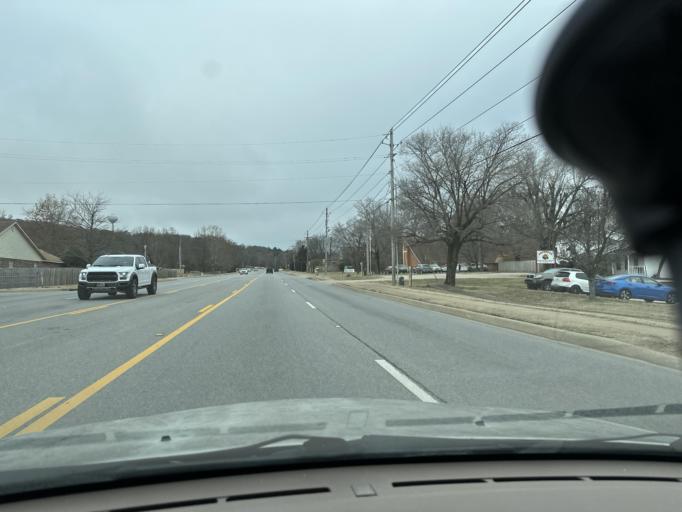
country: US
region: Arkansas
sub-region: Washington County
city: Fayetteville
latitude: 36.0849
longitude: -94.1214
